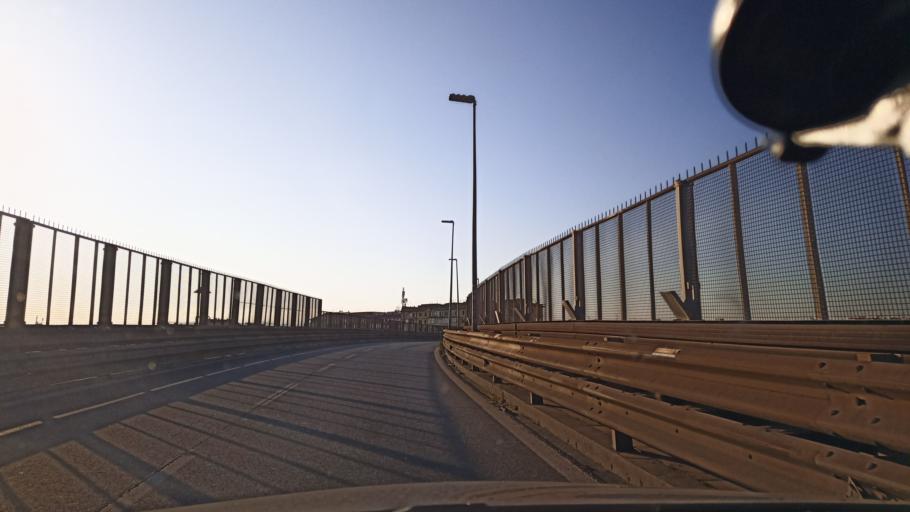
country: IT
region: Latium
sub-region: Citta metropolitana di Roma Capitale
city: Rome
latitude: 41.8931
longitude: 12.5194
